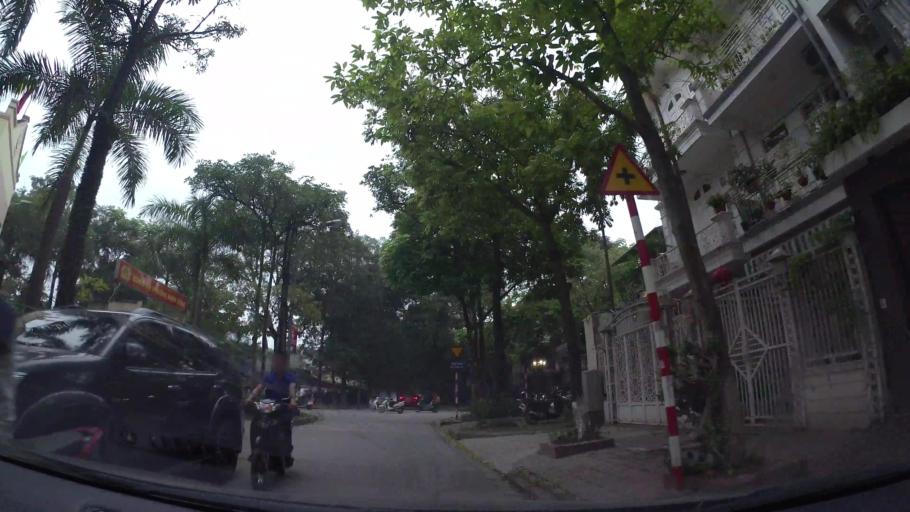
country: VN
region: Ha Noi
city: Hai BaTrung
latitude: 20.9881
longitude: 105.8317
